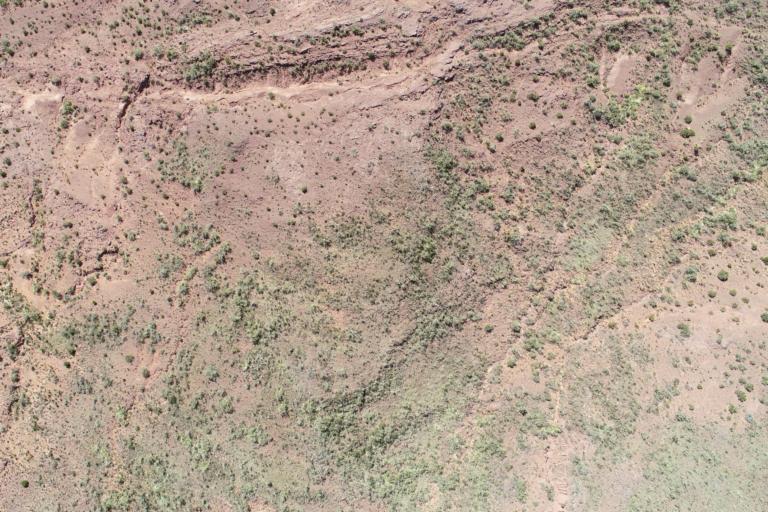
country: BO
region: La Paz
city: Tiahuanaco
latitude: -16.6043
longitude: -68.7562
